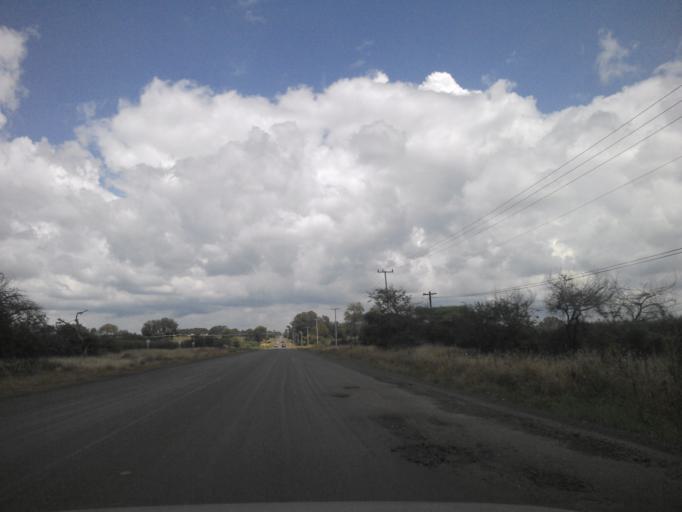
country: MX
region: Jalisco
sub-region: Atotonilco el Alto
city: Ojo de Agua de Moran
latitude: 20.5965
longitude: -102.4938
